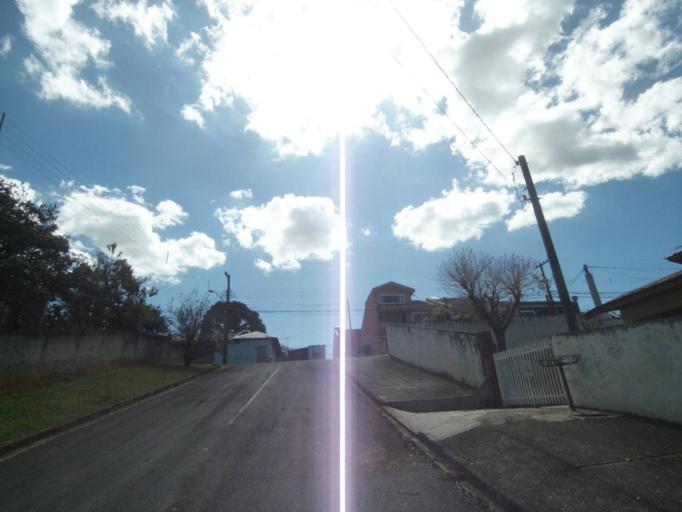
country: BR
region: Parana
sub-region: Curitiba
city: Curitiba
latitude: -25.3810
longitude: -49.2413
